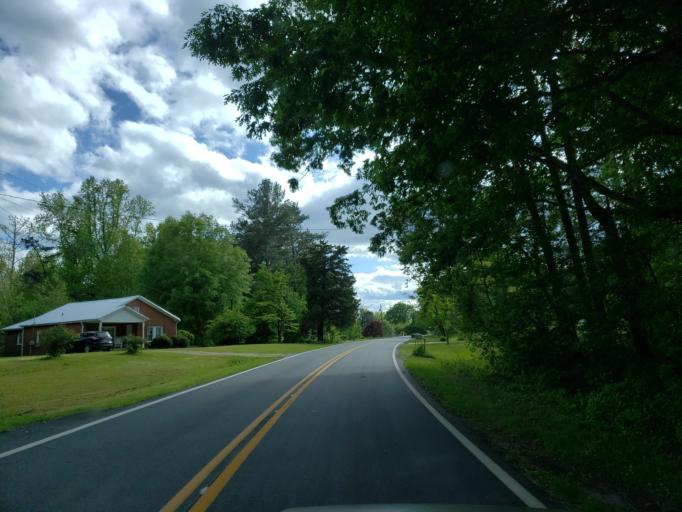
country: US
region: Georgia
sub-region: Carroll County
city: Mount Zion
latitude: 33.6853
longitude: -85.1954
